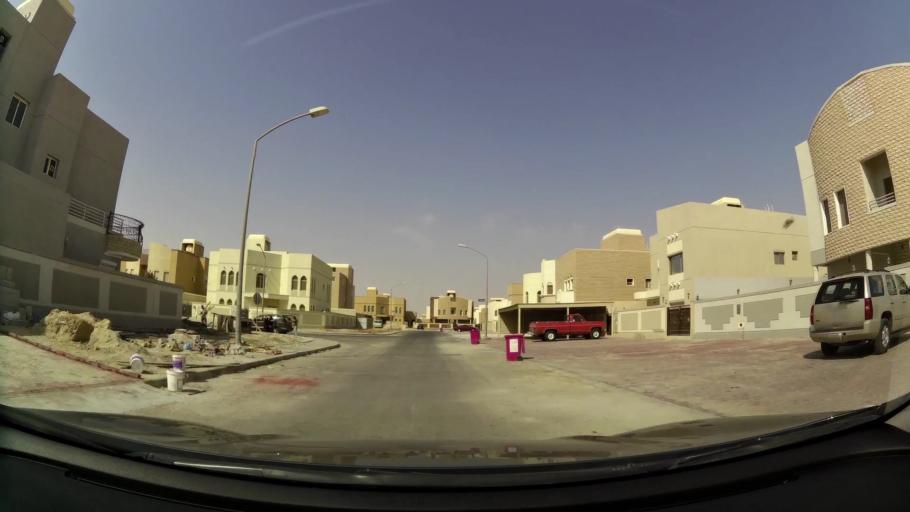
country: KW
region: Al Ahmadi
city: Al Wafrah
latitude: 28.8008
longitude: 48.0566
